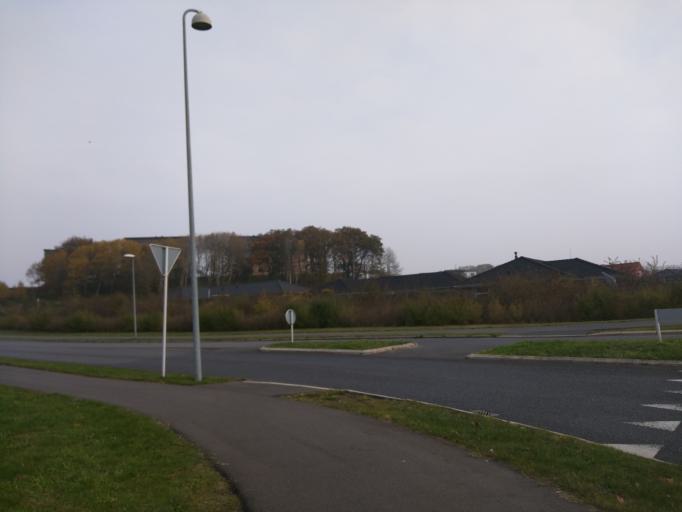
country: DK
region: Central Jutland
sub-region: Viborg Kommune
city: Viborg
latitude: 56.4401
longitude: 9.3581
